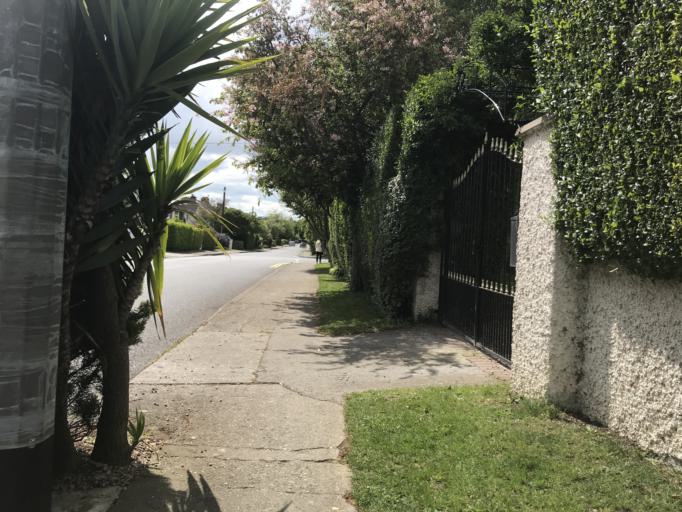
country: IE
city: Booterstown
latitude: 53.2949
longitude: -6.1974
